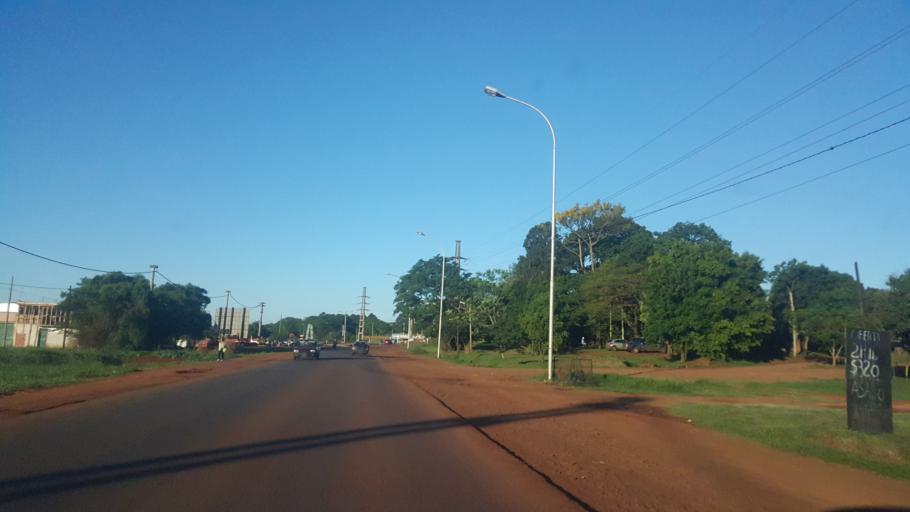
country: AR
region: Misiones
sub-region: Departamento de Capital
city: Posadas
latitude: -27.4269
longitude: -55.9357
